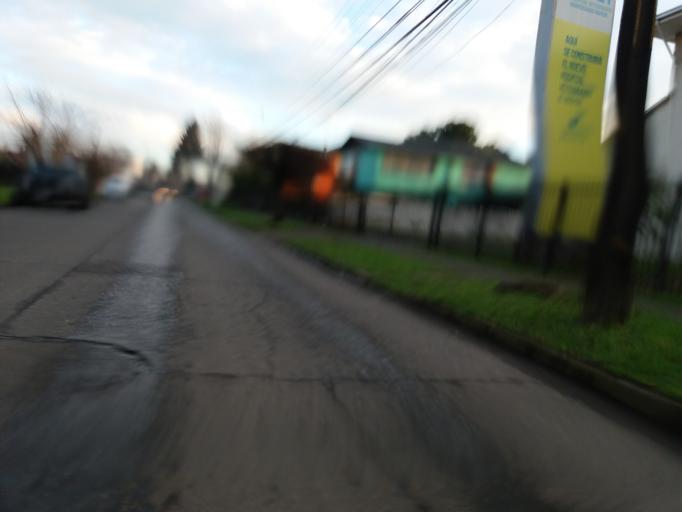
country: CL
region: Araucania
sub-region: Provincia de Cautin
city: Temuco
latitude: -38.7393
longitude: -72.6054
